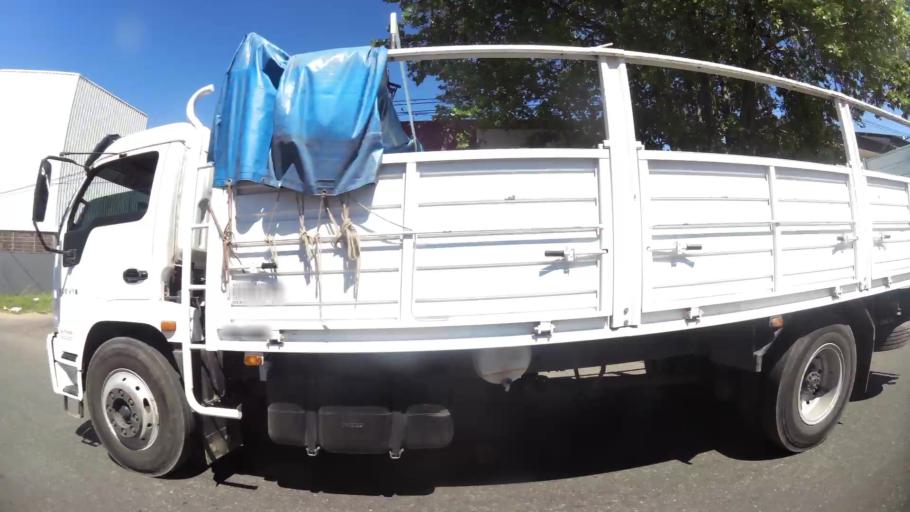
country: AR
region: Santa Fe
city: Perez
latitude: -32.9648
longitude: -60.7117
